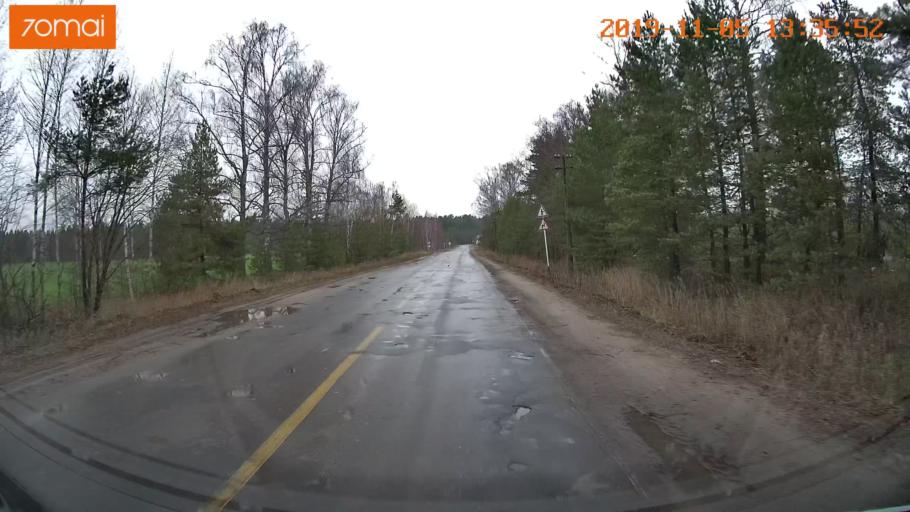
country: RU
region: Ivanovo
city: Shuya
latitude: 56.9107
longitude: 41.3851
